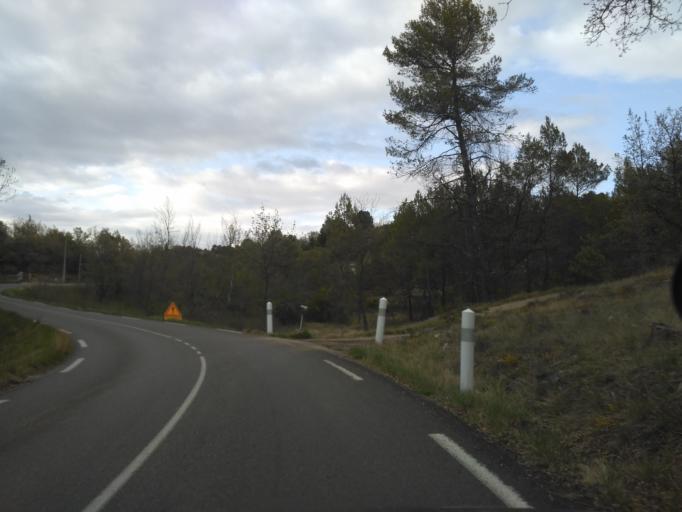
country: FR
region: Provence-Alpes-Cote d'Azur
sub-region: Departement du Var
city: Saint-Julien
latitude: 43.6243
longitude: 5.9436
